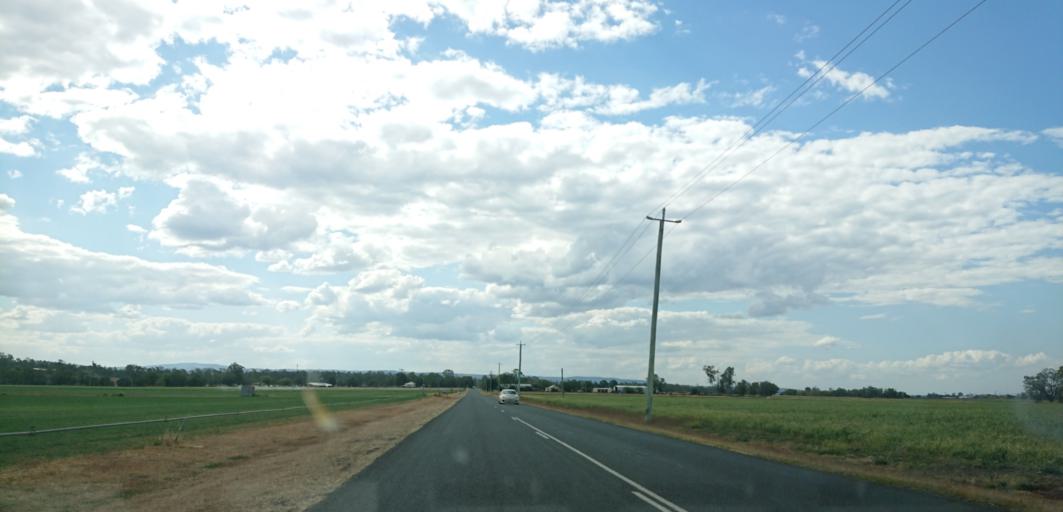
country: AU
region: Queensland
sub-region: Lockyer Valley
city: Gatton
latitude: -27.6178
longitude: 152.2078
